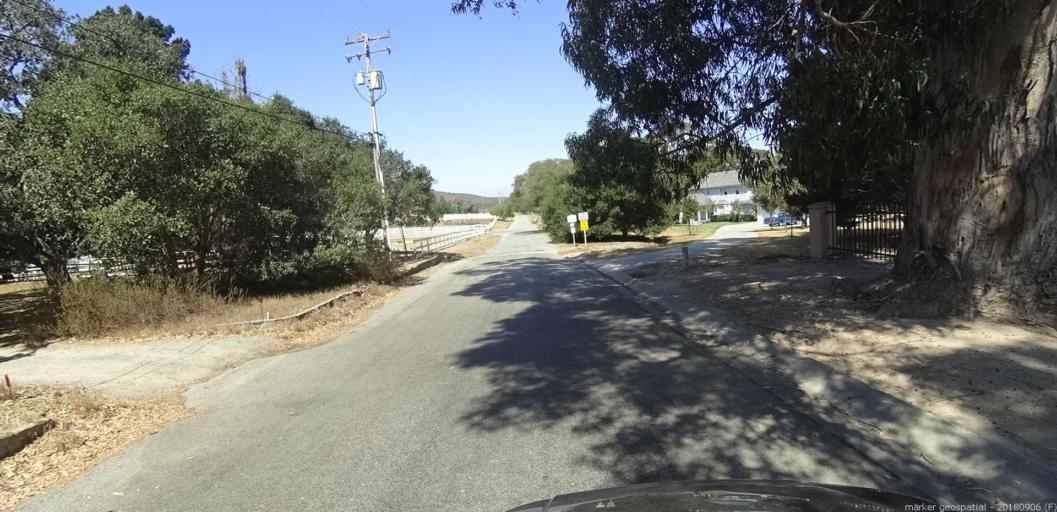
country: US
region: California
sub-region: Monterey County
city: Salinas
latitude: 36.5835
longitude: -121.6319
